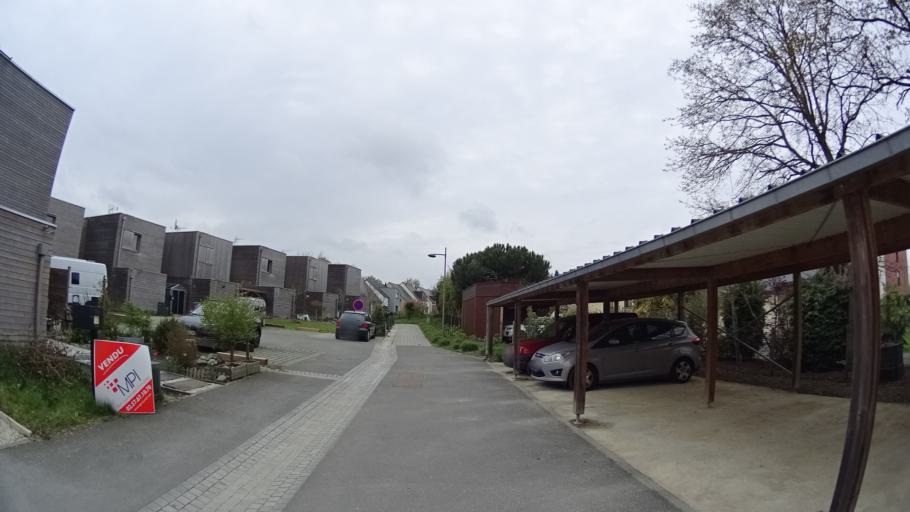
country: FR
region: Brittany
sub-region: Departement d'Ille-et-Vilaine
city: La Chapelle-Thouarault
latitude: 48.1211
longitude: -1.8627
